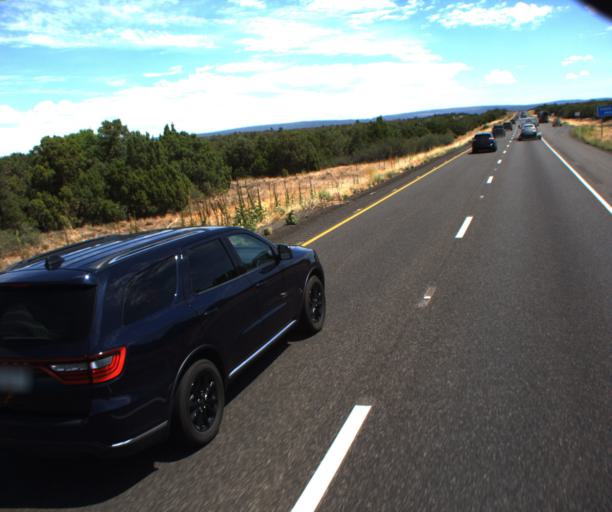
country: US
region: Arizona
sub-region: Yavapai County
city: Village of Oak Creek (Big Park)
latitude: 34.7478
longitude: -111.6796
